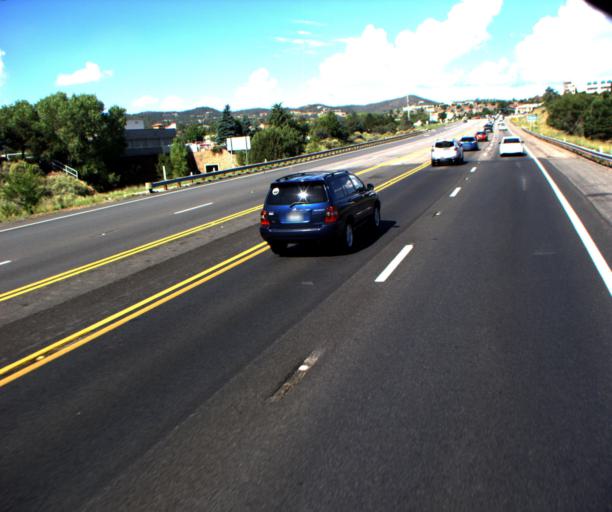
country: US
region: Arizona
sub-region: Yavapai County
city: Prescott
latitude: 34.5482
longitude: -112.3961
